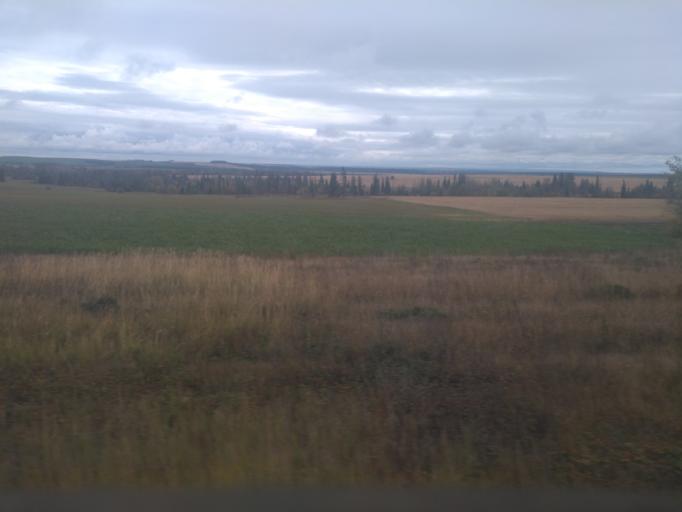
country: RU
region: Udmurtiya
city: Alnashi
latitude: 56.2128
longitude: 52.6264
